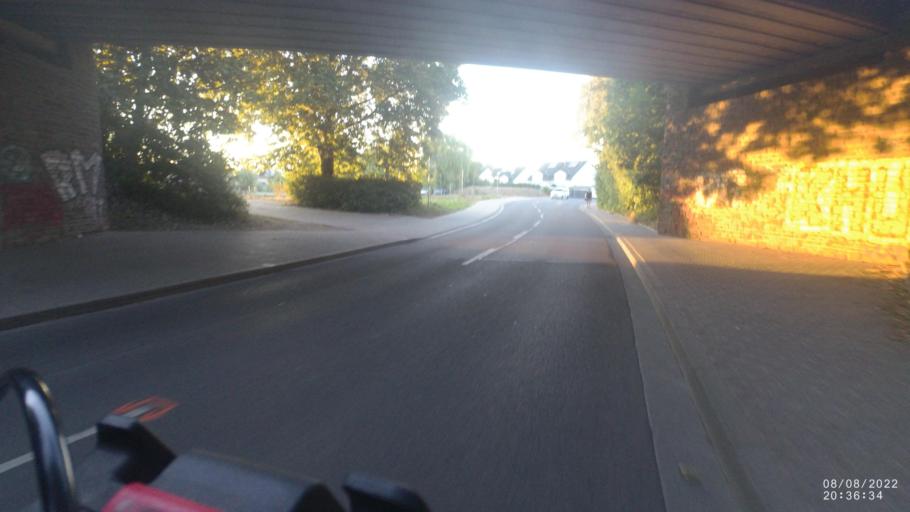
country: DE
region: Rheinland-Pfalz
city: Worrstadt
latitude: 49.8470
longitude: 8.1194
